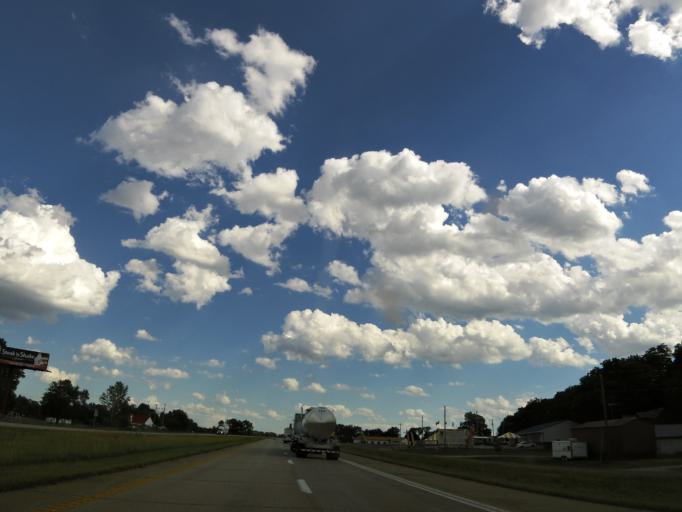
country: US
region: Missouri
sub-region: Clark County
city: Kahoka
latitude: 40.4525
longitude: -91.5687
